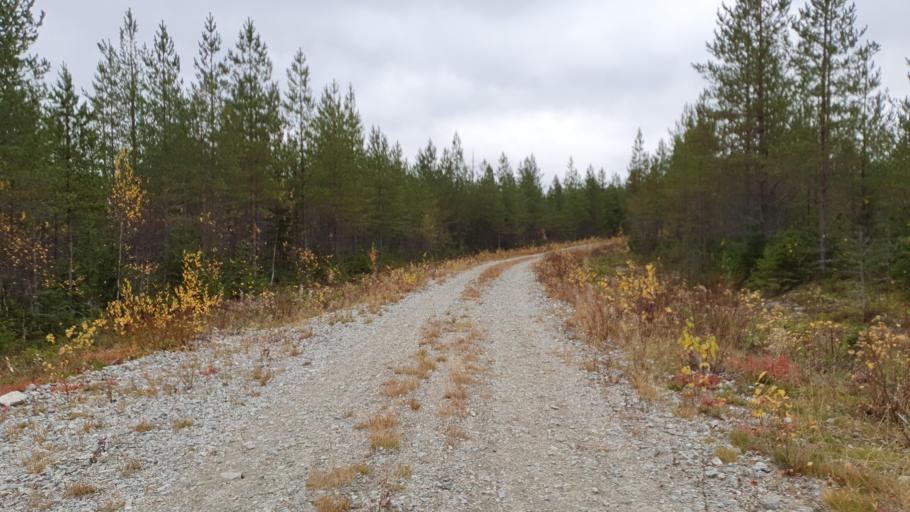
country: FI
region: Kainuu
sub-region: Kehys-Kainuu
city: Kuhmo
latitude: 64.4502
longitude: 29.5983
